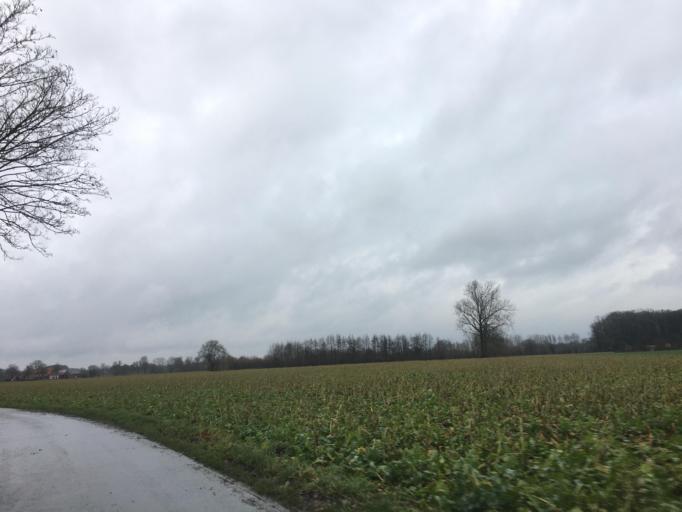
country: DE
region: North Rhine-Westphalia
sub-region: Regierungsbezirk Munster
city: Nordwalde
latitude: 52.0967
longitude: 7.4845
